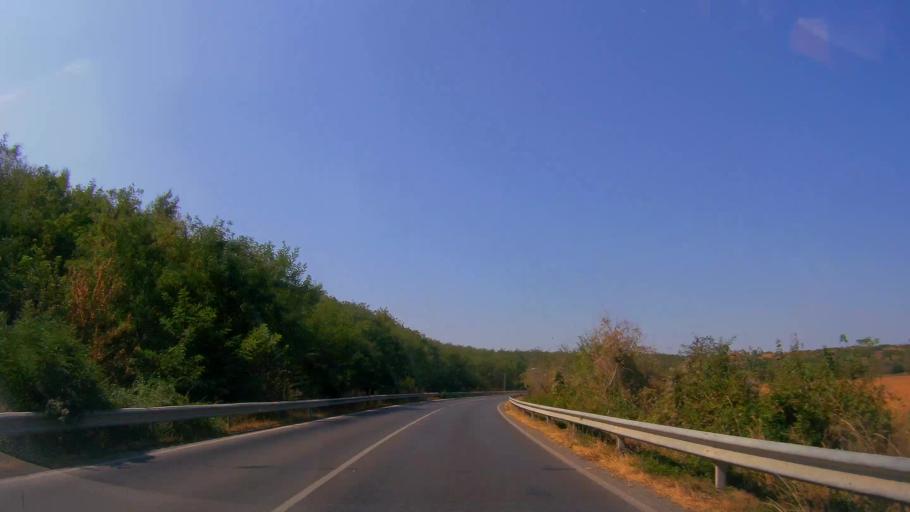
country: BG
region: Razgrad
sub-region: Obshtina Tsar Kaloyan
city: Tsar Kaloyan
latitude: 43.6149
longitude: 26.2164
